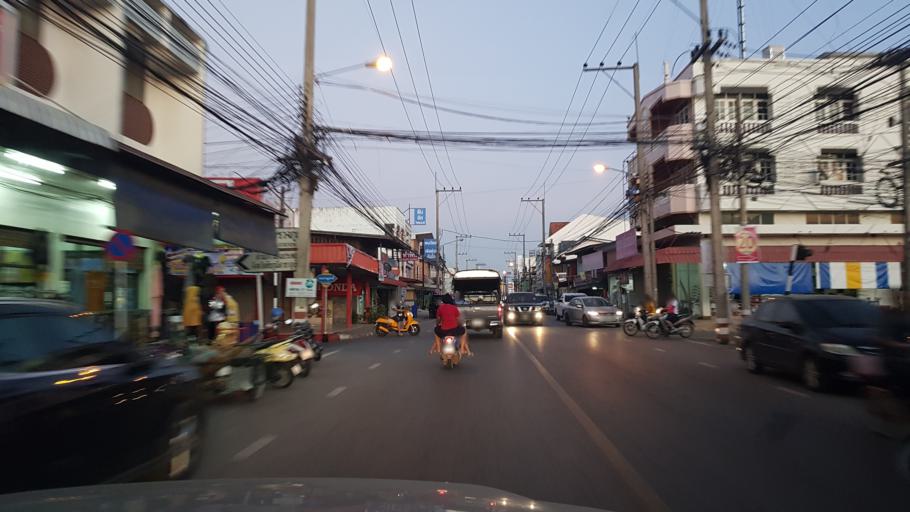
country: TH
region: Chaiyaphum
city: Phu Khiao
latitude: 16.3662
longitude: 102.1351
